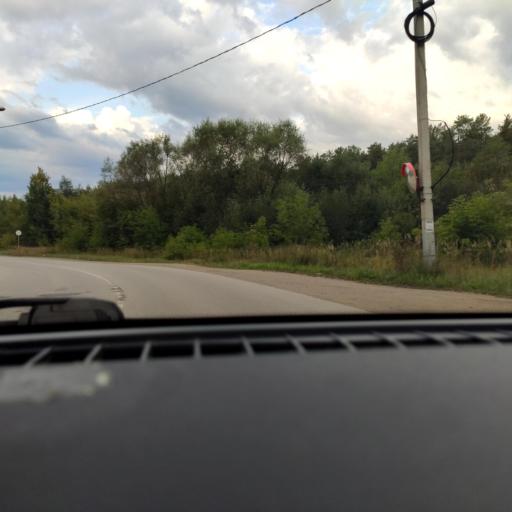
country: RU
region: Perm
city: Perm
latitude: 58.0455
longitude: 56.2737
